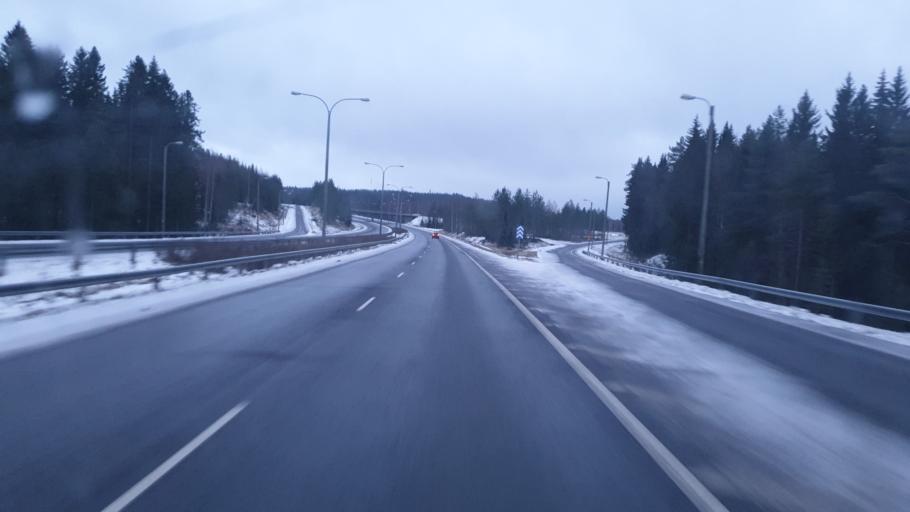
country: FI
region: Northern Savo
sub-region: Kuopio
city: Siilinjaervi
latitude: 63.0218
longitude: 27.6599
